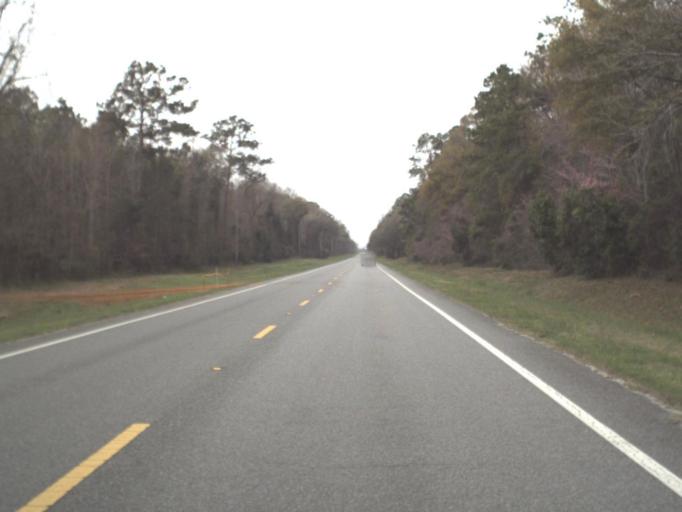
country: US
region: Florida
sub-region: Wakulla County
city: Crawfordville
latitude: 30.1519
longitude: -84.2734
